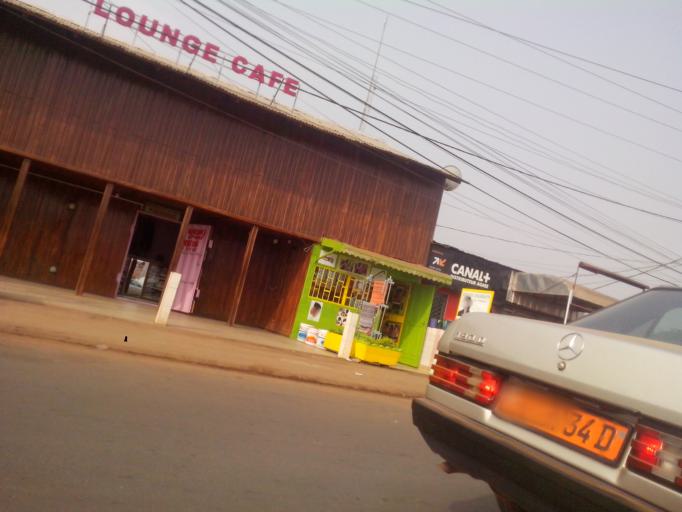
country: CM
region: Centre
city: Yaounde
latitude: 3.8486
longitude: 11.4958
